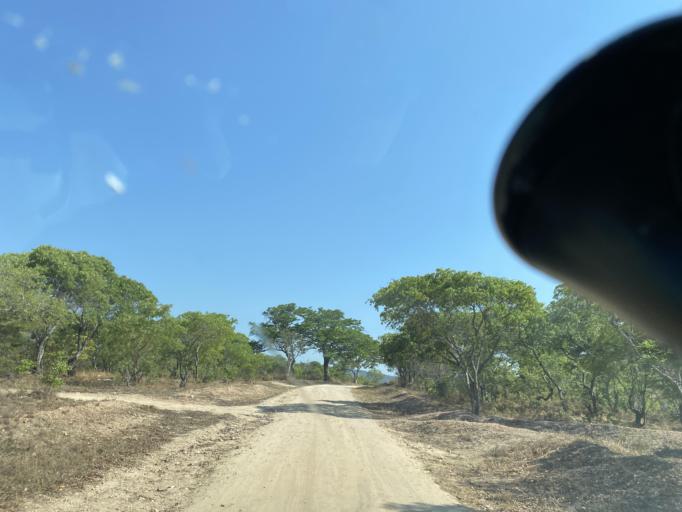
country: ZM
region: Lusaka
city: Chongwe
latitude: -15.2272
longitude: 28.8397
